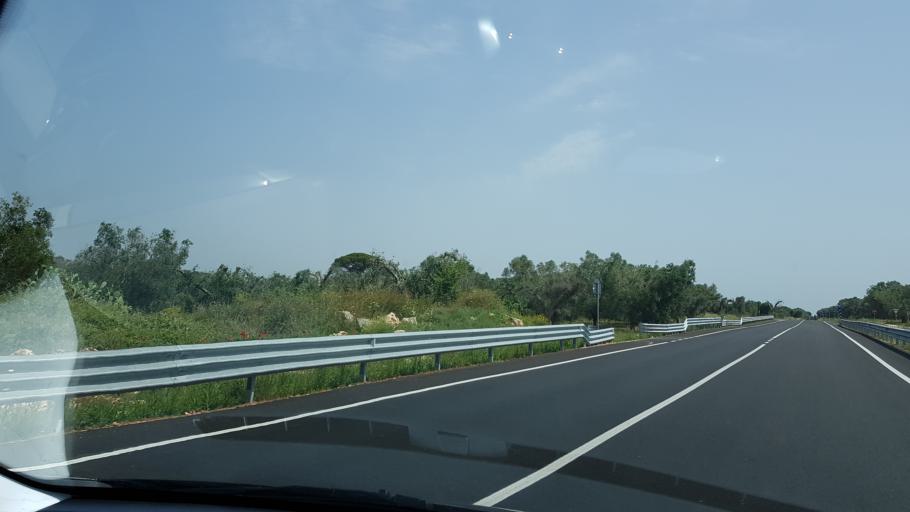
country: IT
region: Apulia
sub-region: Provincia di Brindisi
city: San Pancrazio Salentino
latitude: 40.4649
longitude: 17.8385
